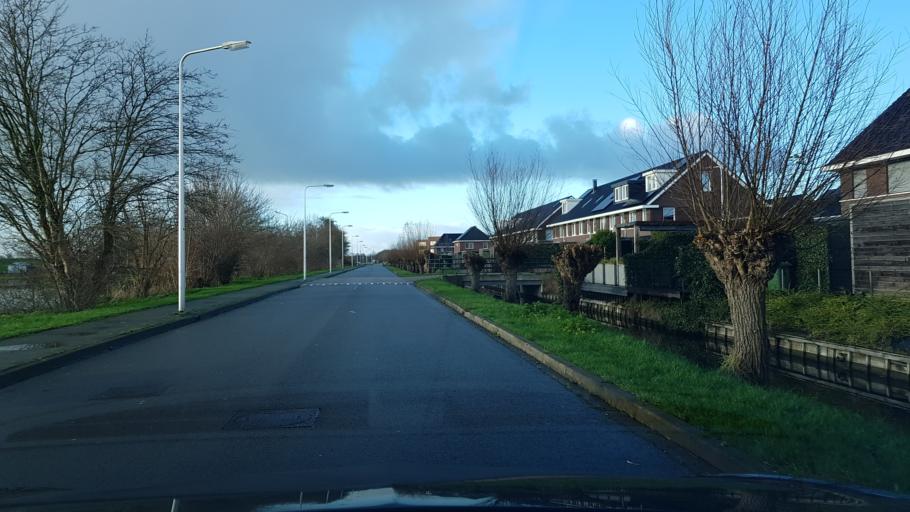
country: NL
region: South Holland
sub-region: Gemeente Kaag en Braassem
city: Leimuiden
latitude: 52.2212
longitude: 4.6627
